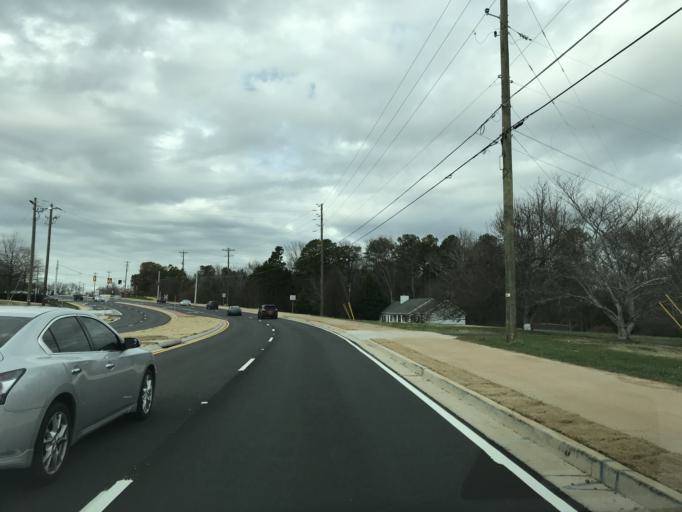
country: US
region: Georgia
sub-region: Forsyth County
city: Cumming
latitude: 34.1221
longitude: -84.1667
